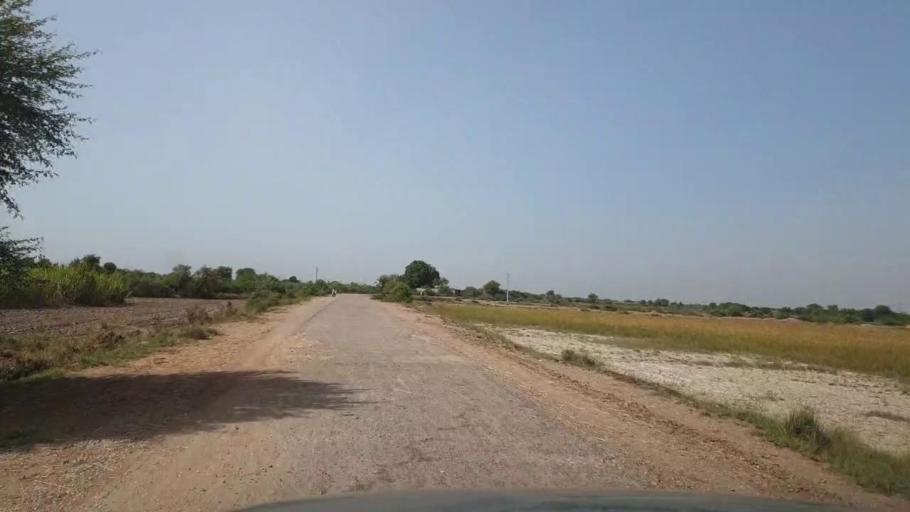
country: PK
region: Sindh
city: Tando Muhammad Khan
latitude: 25.1559
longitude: 68.4011
